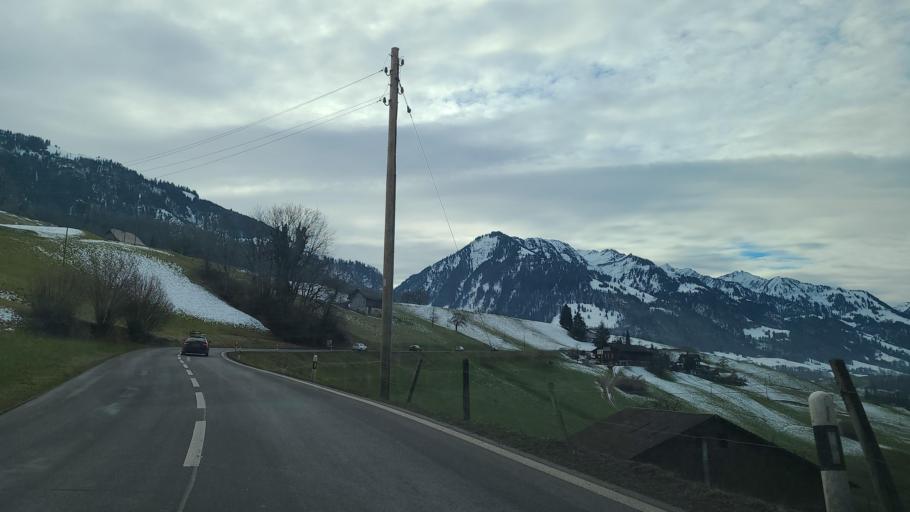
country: CH
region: Obwalden
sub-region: Obwalden
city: Kerns
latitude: 46.8941
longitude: 8.2774
